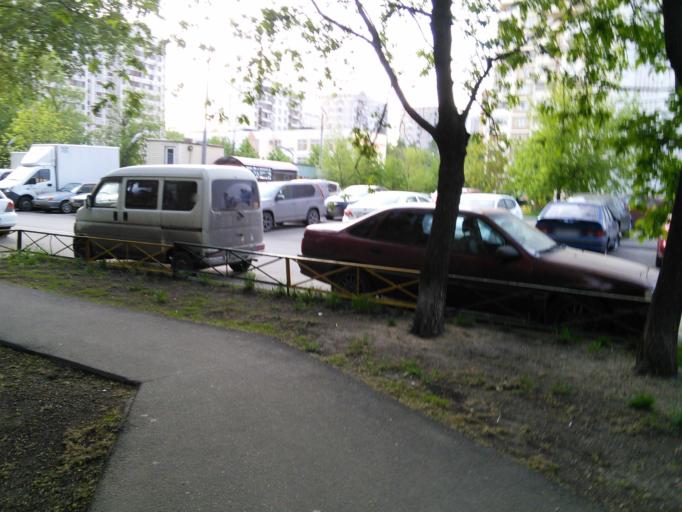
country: RU
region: Moscow
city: Mar'ina Roshcha
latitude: 55.8022
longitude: 37.6150
